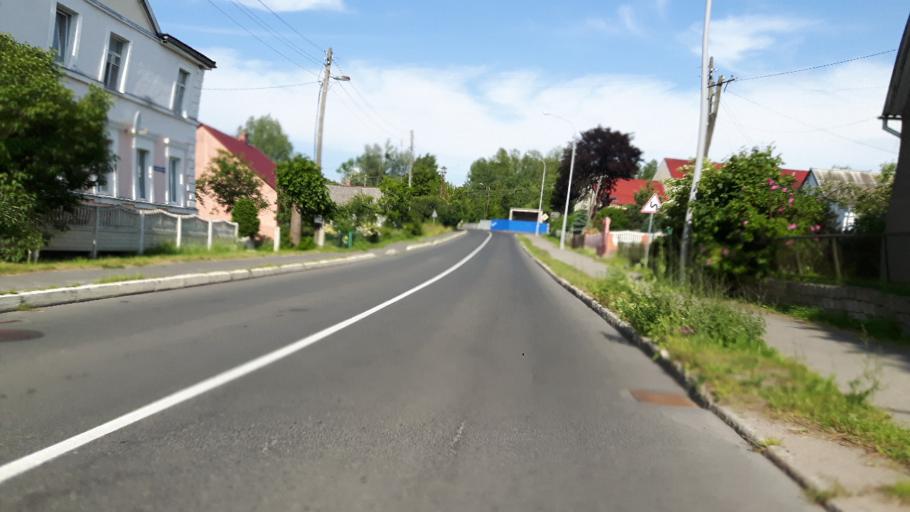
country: RU
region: Kaliningrad
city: Mamonovo
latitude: 54.4602
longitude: 19.9336
